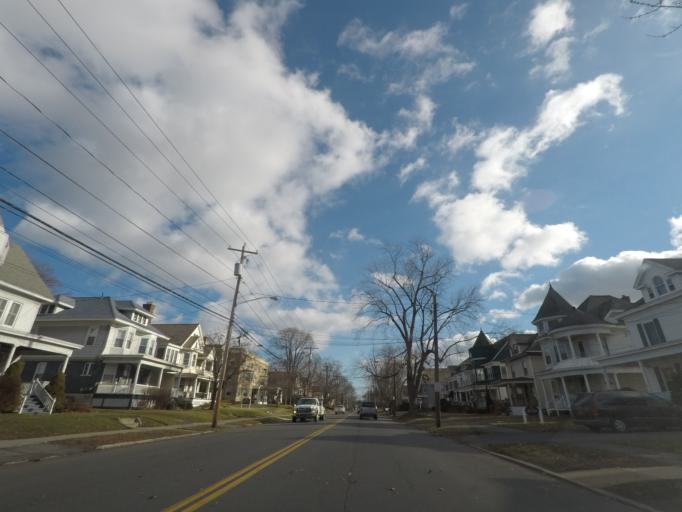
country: US
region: New York
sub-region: Schenectady County
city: Schenectady
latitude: 42.8078
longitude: -73.9124
